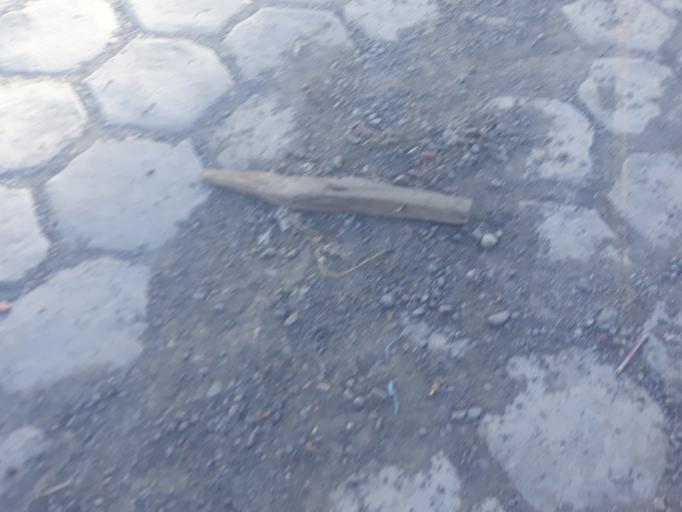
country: BO
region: La Paz
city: Achacachi
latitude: -16.0496
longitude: -68.6867
